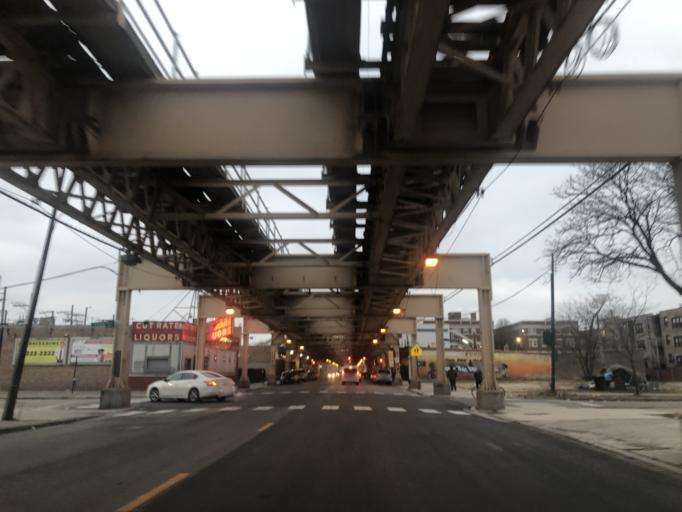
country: US
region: Illinois
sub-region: Cook County
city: Chicago
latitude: 41.7803
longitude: -87.6138
